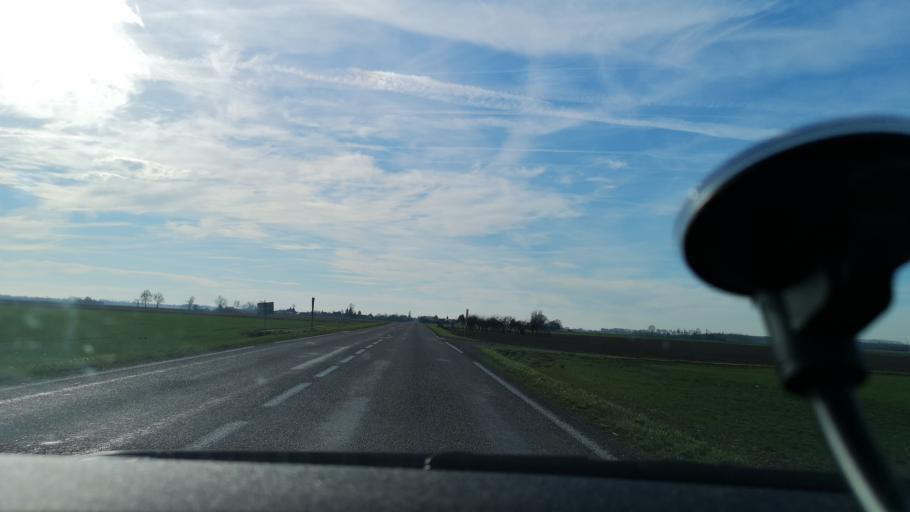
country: FR
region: Franche-Comte
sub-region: Departement du Jura
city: Petit-Noir
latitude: 46.9764
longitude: 5.3112
